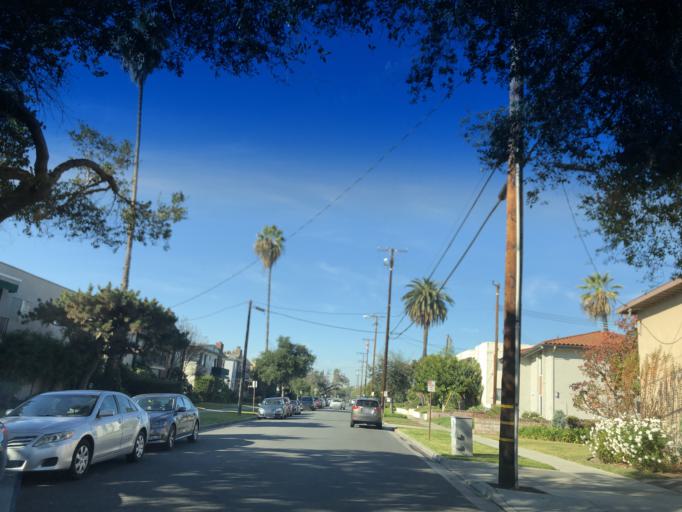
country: US
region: California
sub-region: Los Angeles County
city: San Gabriel
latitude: 34.1012
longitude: -118.0975
